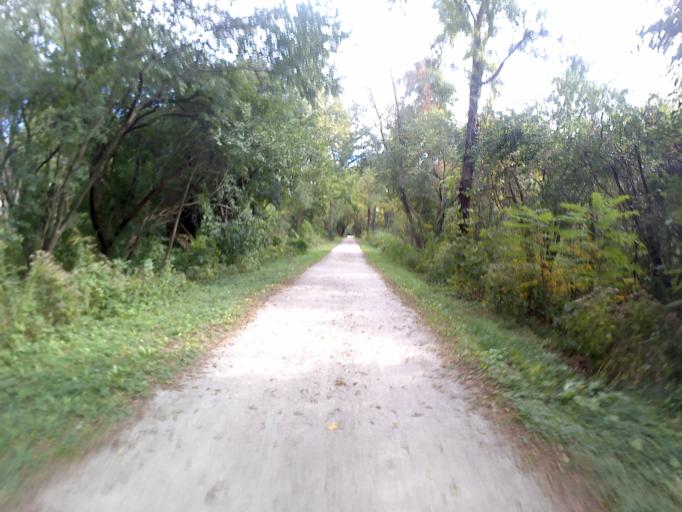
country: US
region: Illinois
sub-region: DuPage County
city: West Chicago
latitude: 41.9242
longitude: -88.2121
